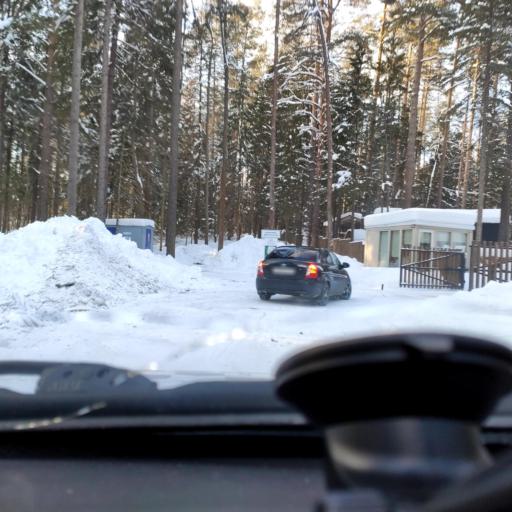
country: RU
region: Perm
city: Perm
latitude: 58.0728
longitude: 56.2607
